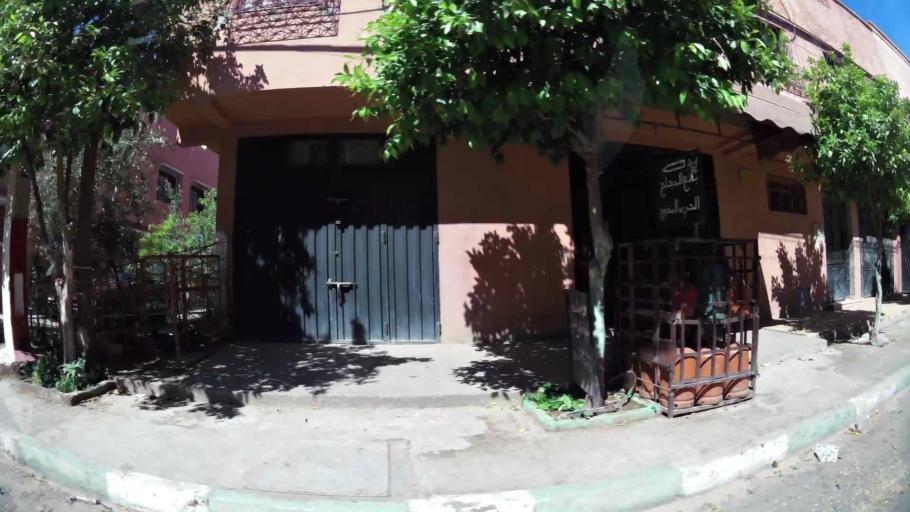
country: MA
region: Marrakech-Tensift-Al Haouz
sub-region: Marrakech
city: Marrakesh
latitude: 31.6447
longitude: -8.1145
